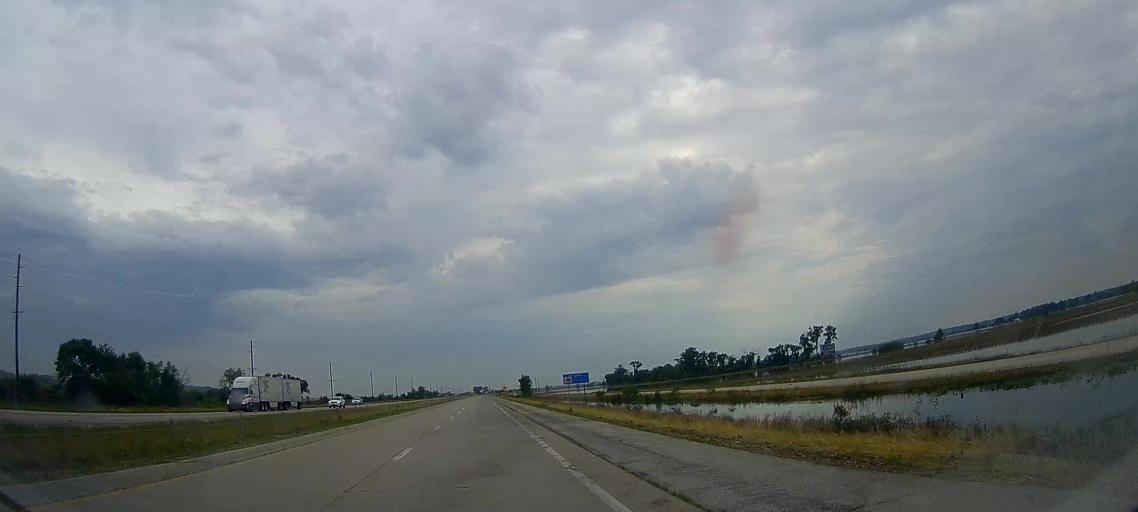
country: US
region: Iowa
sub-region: Pottawattamie County
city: Carter Lake
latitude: 41.3730
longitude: -95.8996
